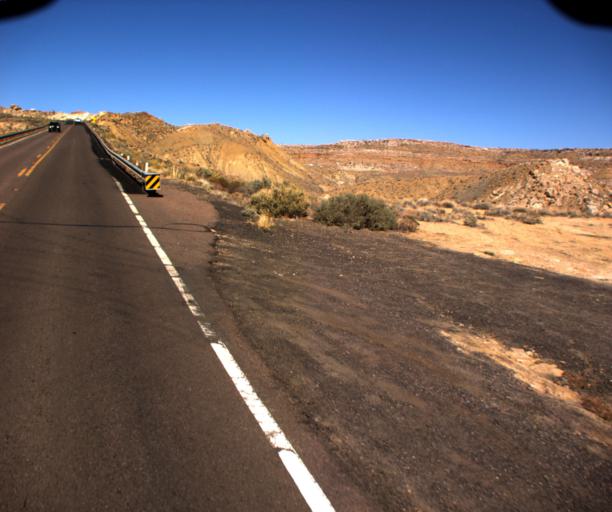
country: US
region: Arizona
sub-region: Navajo County
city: First Mesa
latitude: 35.8032
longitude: -110.5152
